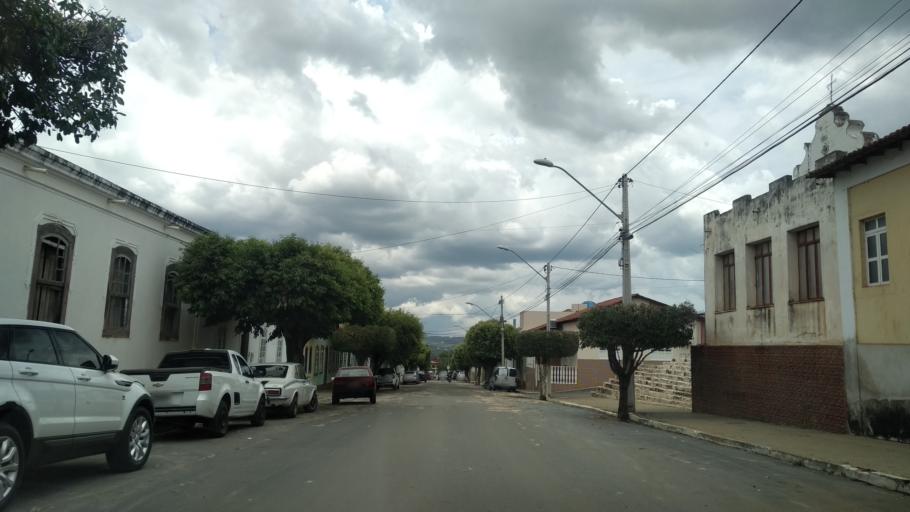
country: BR
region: Bahia
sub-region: Caetite
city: Caetite
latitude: -14.0697
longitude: -42.4875
